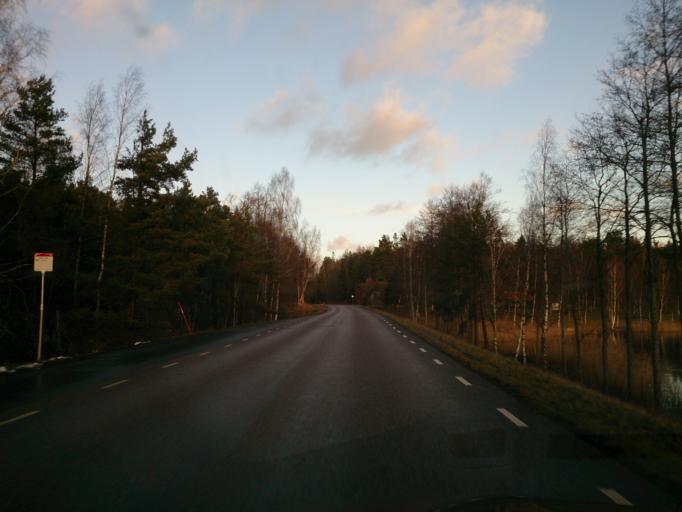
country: SE
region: OEstergoetland
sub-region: Atvidabergs Kommun
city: Atvidaberg
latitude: 58.2433
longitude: 16.0094
